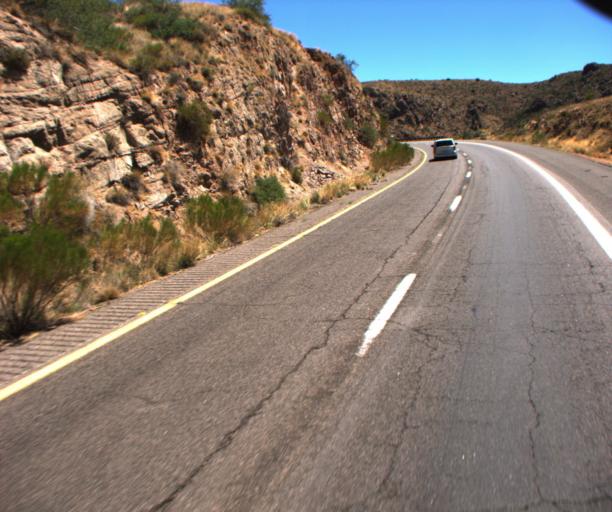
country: US
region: Arizona
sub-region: Gila County
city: Tonto Basin
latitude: 33.8374
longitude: -111.4706
